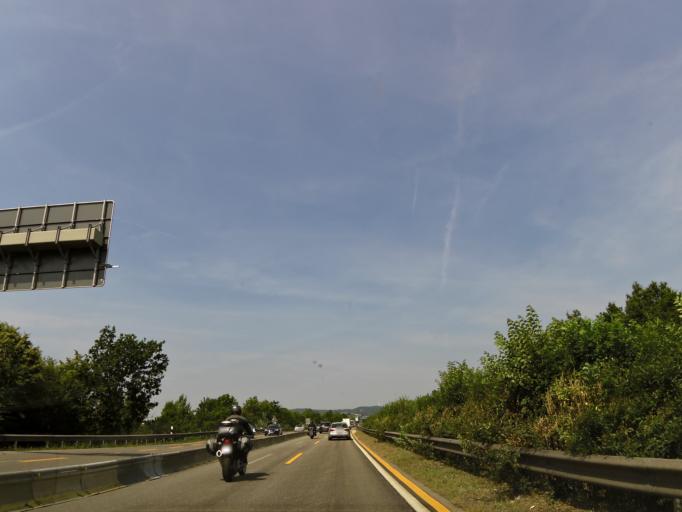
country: DE
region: Rheinland-Pfalz
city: Mendig
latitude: 50.3854
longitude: 7.2713
